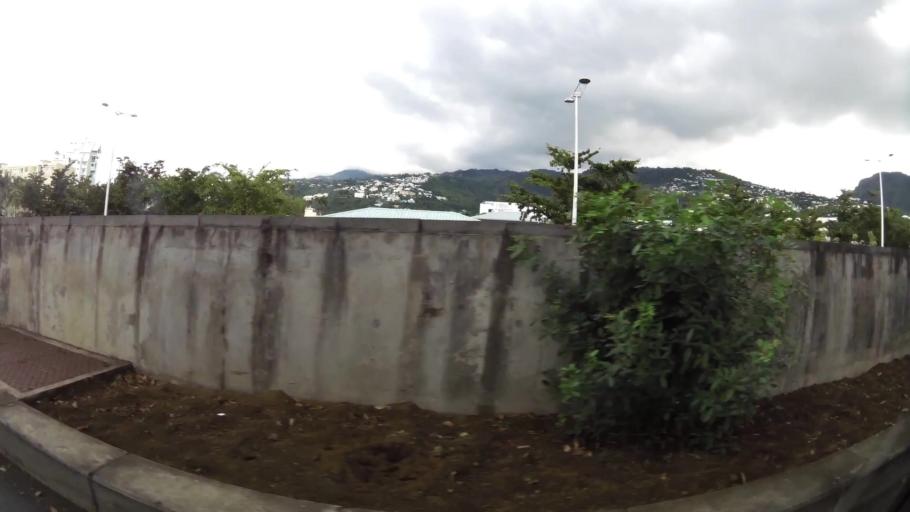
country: RE
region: Reunion
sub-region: Reunion
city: Saint-Denis
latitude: -20.8908
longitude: 55.4566
